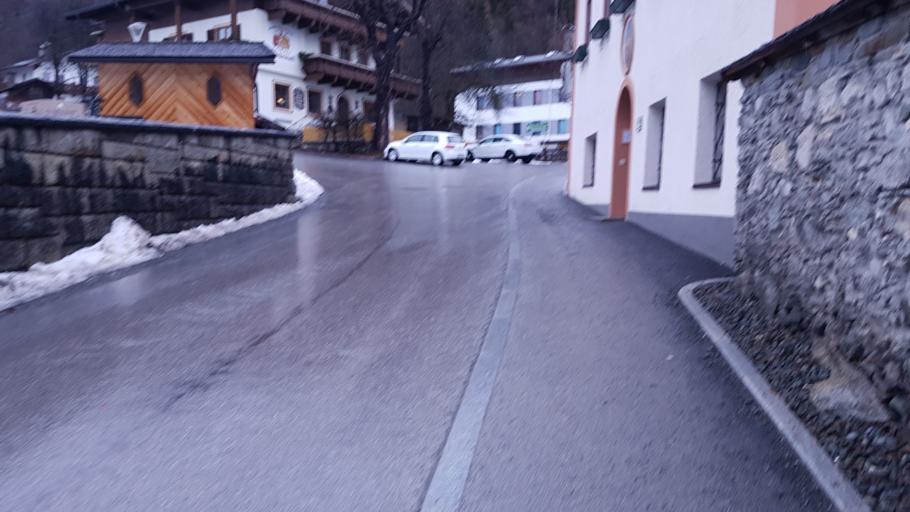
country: AT
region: Salzburg
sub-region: Politischer Bezirk Zell am See
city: Neukirchen am Grossvenediger
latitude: 47.2541
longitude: 12.2775
